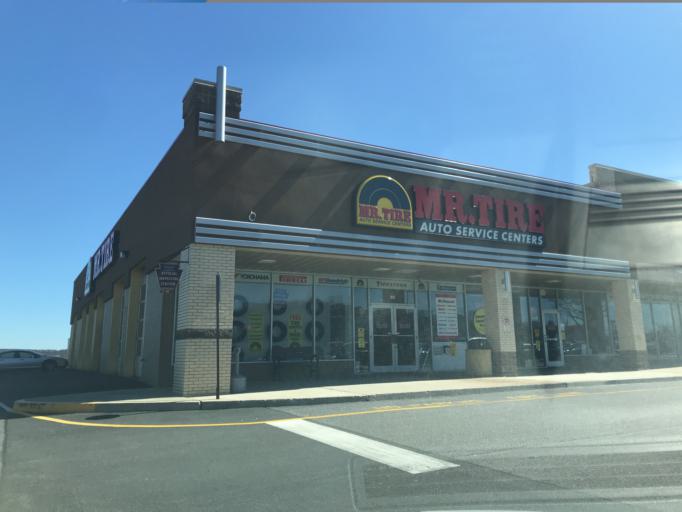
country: US
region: Pennsylvania
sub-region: York County
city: Shrewsbury
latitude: 39.7704
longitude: -76.6699
